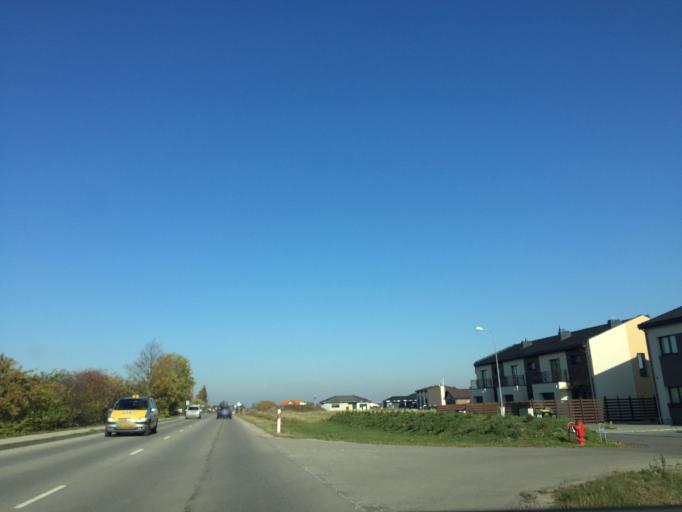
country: LT
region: Klaipedos apskritis
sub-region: Klaipeda
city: Klaipeda
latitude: 55.7405
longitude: 21.1925
